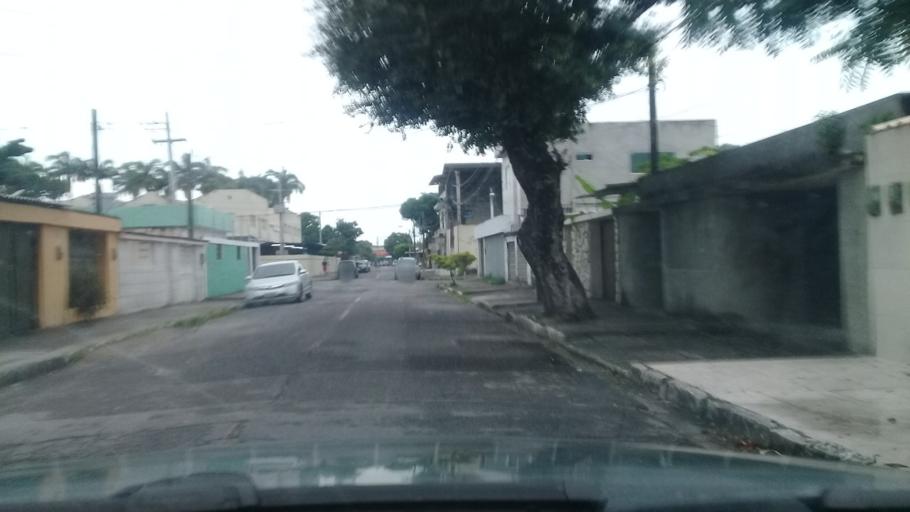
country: BR
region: Pernambuco
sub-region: Recife
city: Recife
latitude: -8.1106
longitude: -34.9246
